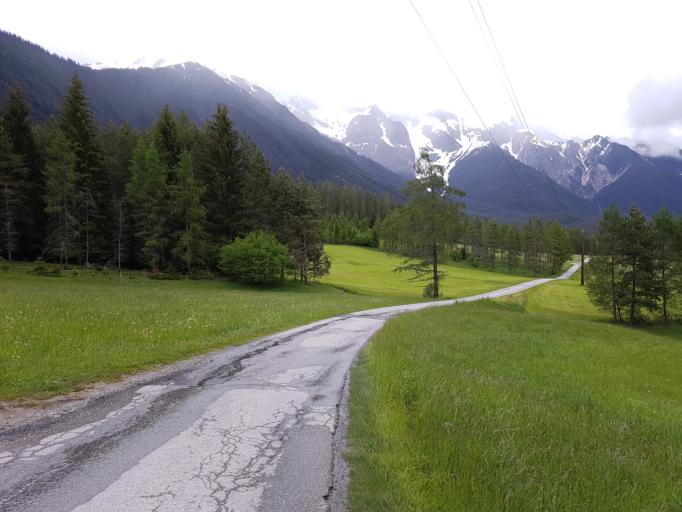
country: AT
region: Tyrol
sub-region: Politischer Bezirk Imst
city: Obsteig
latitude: 47.3033
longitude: 10.9354
